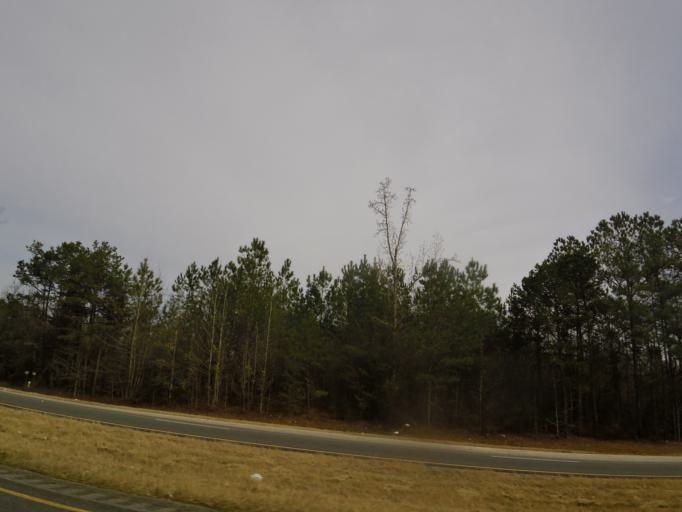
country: US
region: Alabama
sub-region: Dale County
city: Ozark
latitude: 31.5577
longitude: -85.7473
